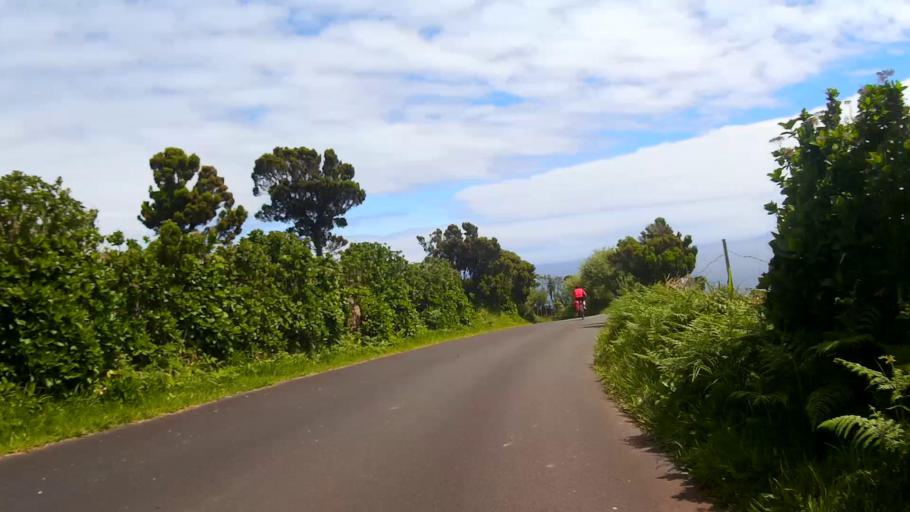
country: PT
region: Azores
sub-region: Horta
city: Horta
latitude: 38.5518
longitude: -28.6721
